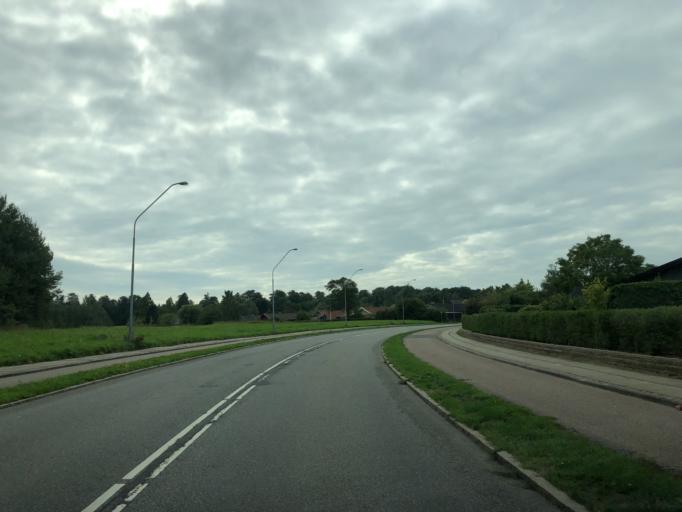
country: DK
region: South Denmark
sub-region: Sonderborg Kommune
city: Sonderborg
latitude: 54.9003
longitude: 9.8239
